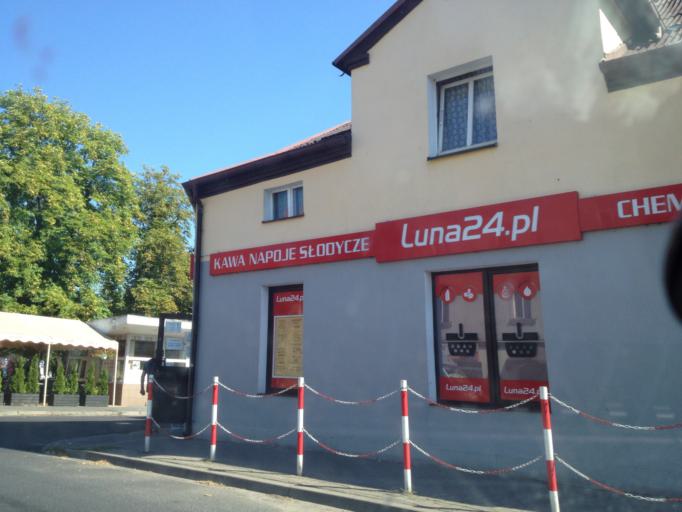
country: PL
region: Greater Poland Voivodeship
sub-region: Powiat sredzki
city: Zaniemysl
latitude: 52.1567
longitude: 17.1601
